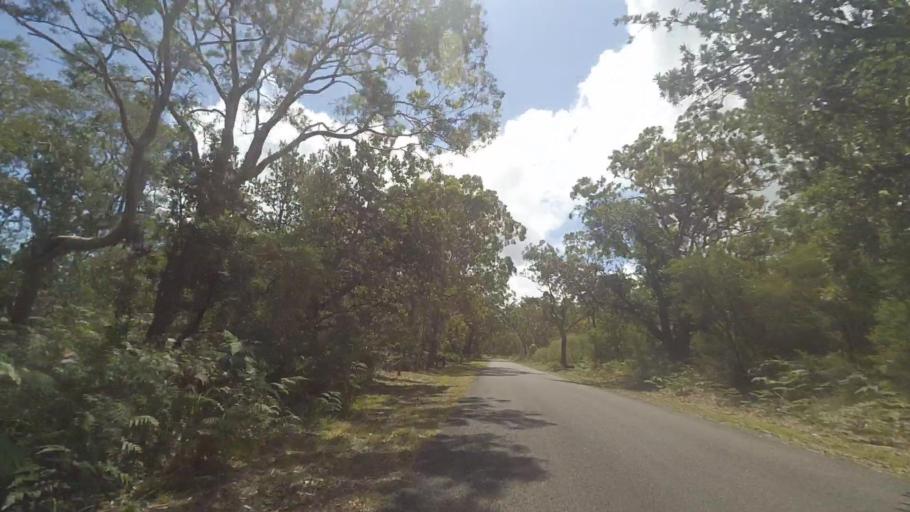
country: AU
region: New South Wales
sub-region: Great Lakes
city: Bulahdelah
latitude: -32.5054
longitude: 152.3137
